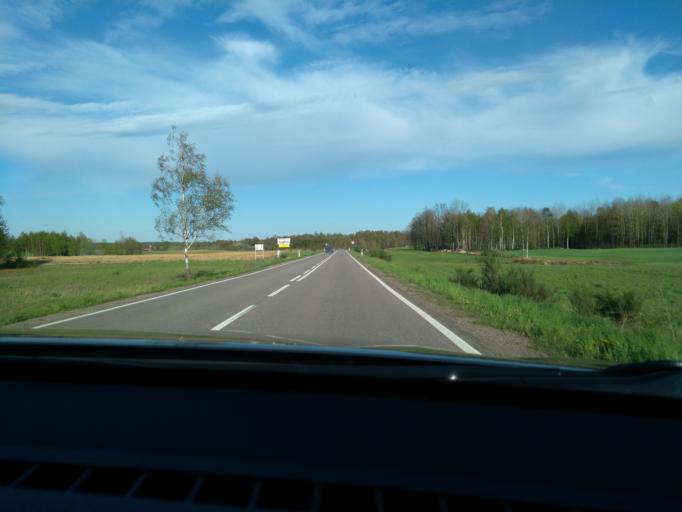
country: PL
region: Pomeranian Voivodeship
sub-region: Powiat leborski
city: Cewice
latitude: 54.3383
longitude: 17.7011
